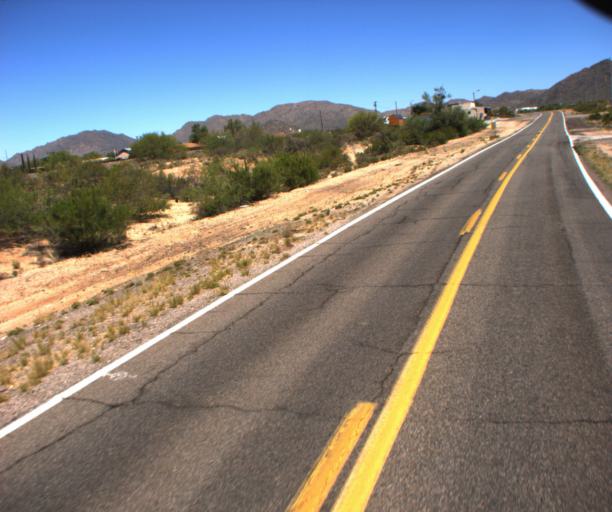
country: US
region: Arizona
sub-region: Yavapai County
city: Congress
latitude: 34.1524
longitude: -112.8435
